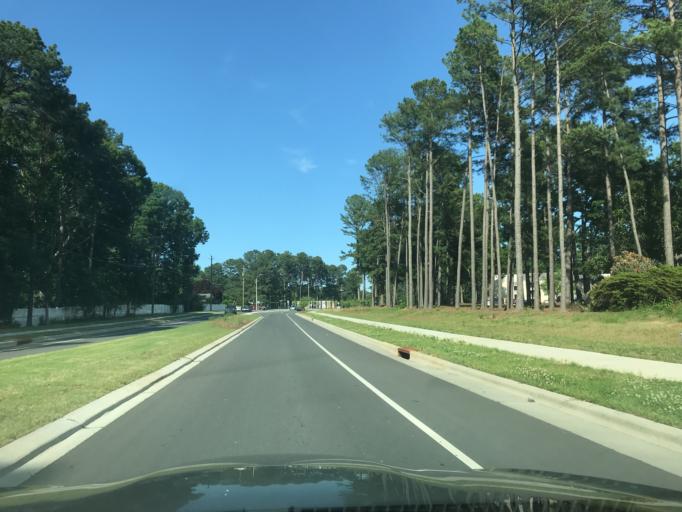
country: US
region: North Carolina
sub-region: Wake County
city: West Raleigh
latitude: 35.8697
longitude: -78.6290
